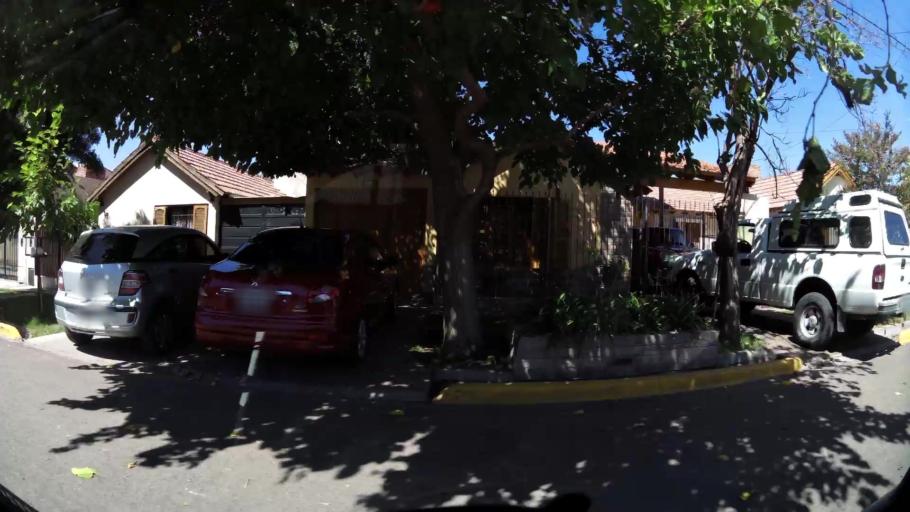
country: AR
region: Mendoza
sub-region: Departamento de Godoy Cruz
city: Godoy Cruz
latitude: -32.9762
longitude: -68.8544
